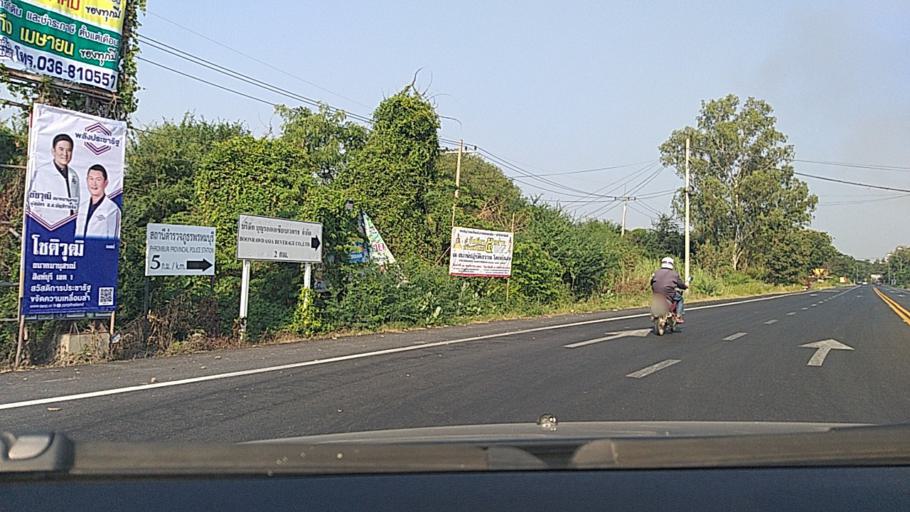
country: TH
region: Sing Buri
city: Phrom Buri
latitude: 14.7599
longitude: 100.4347
